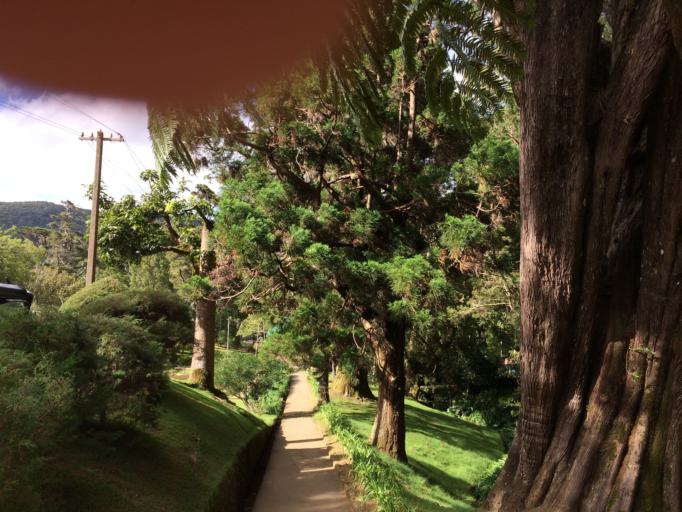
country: LK
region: Central
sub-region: Nuwara Eliya District
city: Nuwara Eliya
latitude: 6.9249
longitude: 80.8219
